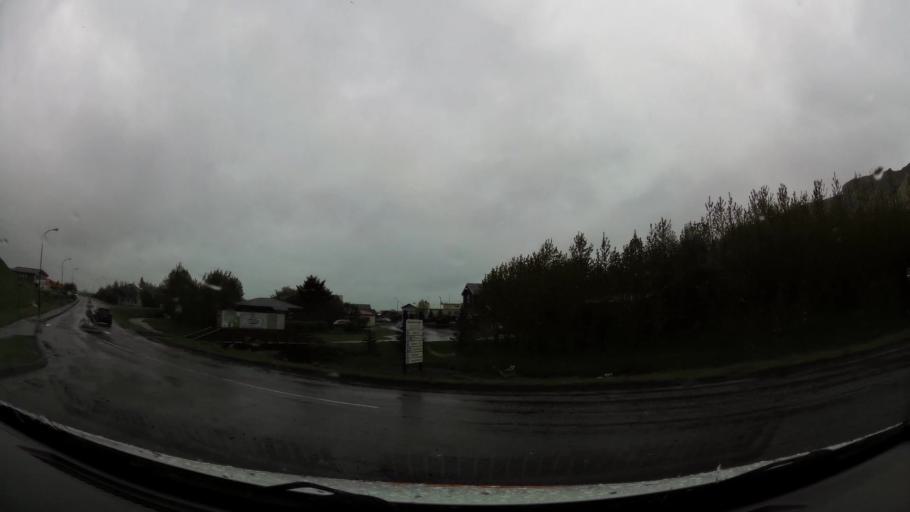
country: IS
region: South
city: Vestmannaeyjar
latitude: 63.4206
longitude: -19.0087
